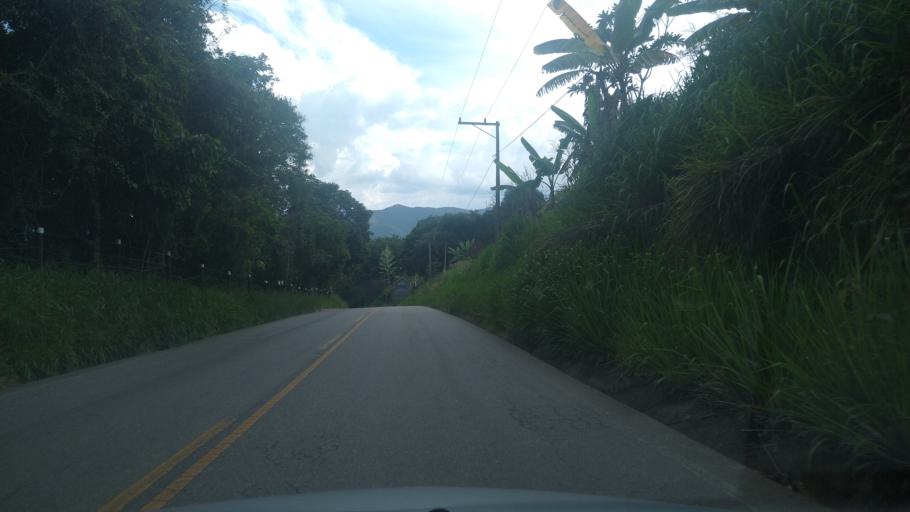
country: BR
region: Minas Gerais
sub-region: Extrema
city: Extrema
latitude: -22.8061
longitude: -46.3142
